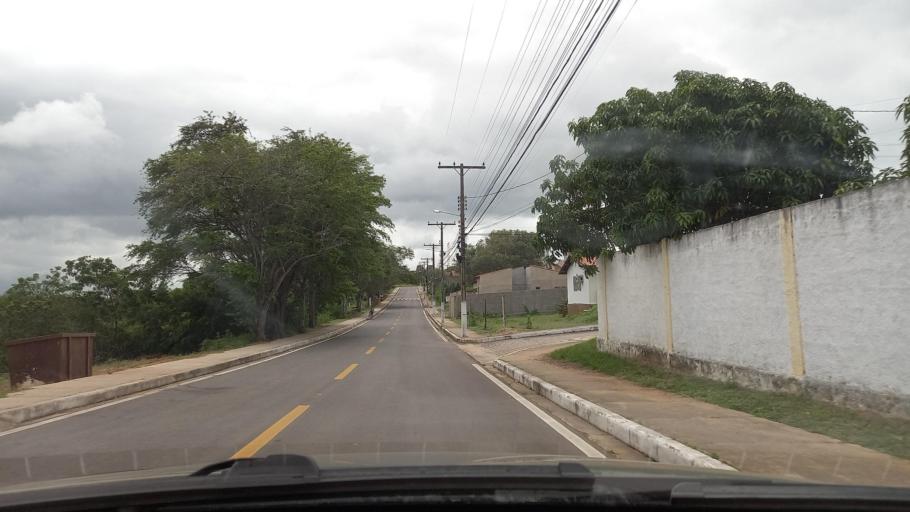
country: BR
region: Sergipe
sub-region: Caninde De Sao Francisco
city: Caninde de Sao Francisco
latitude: -9.6208
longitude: -37.7661
